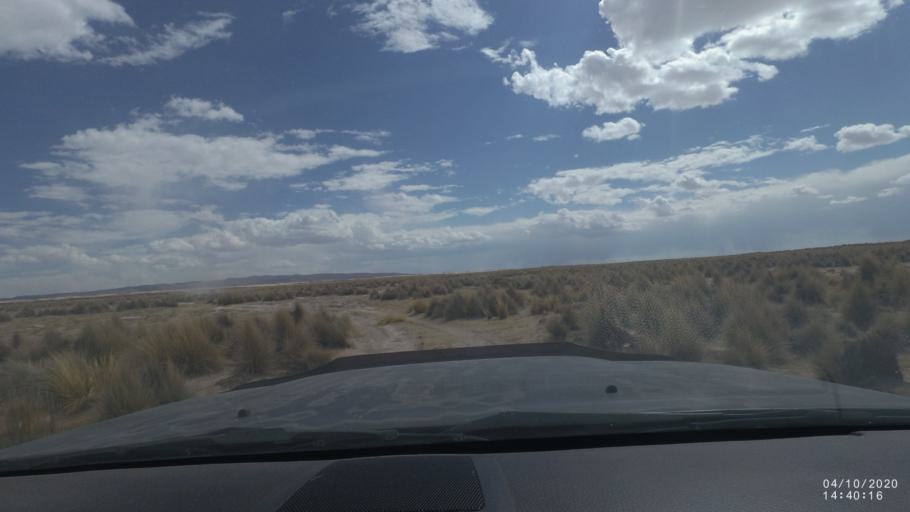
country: BO
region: Oruro
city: Poopo
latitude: -18.6788
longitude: -67.4899
